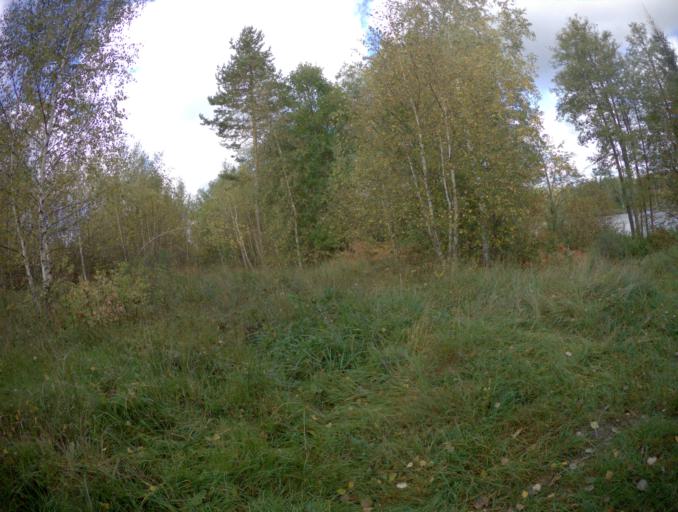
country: RU
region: Moskovskaya
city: Baksheyevo
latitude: 55.7338
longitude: 39.8231
